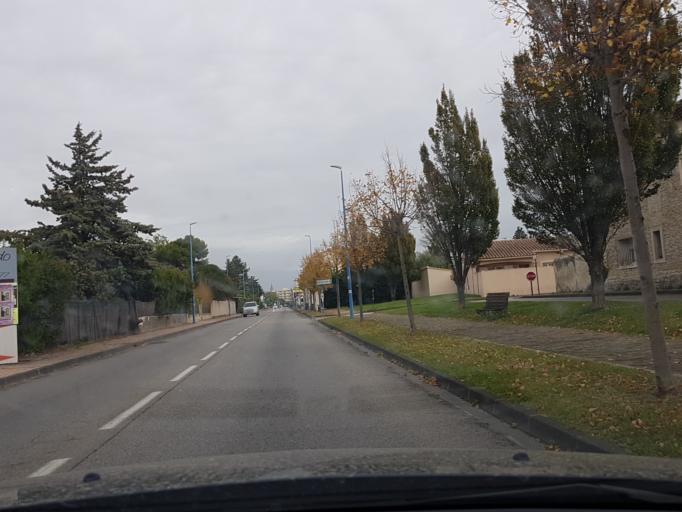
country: FR
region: Provence-Alpes-Cote d'Azur
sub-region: Departement du Vaucluse
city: Carpentras
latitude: 44.0469
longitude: 5.0313
